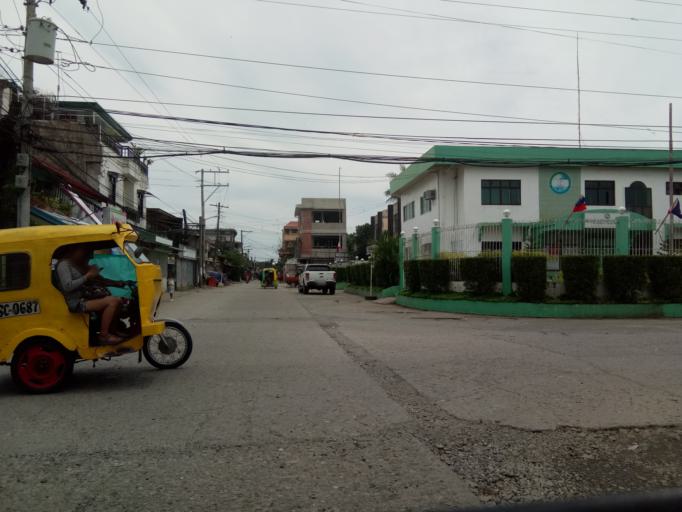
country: PH
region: Caraga
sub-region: Province of Surigao del Norte
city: Surigao
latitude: 9.7851
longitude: 125.4879
